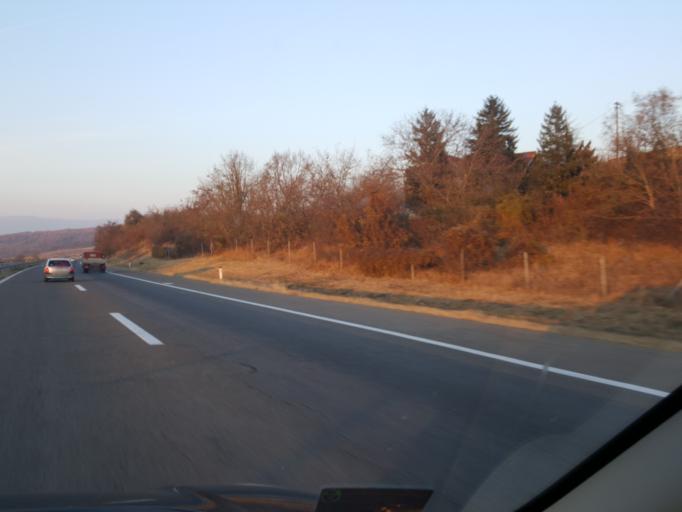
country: RS
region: Central Serbia
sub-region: Nisavski Okrug
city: Nis
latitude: 43.4252
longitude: 21.7969
